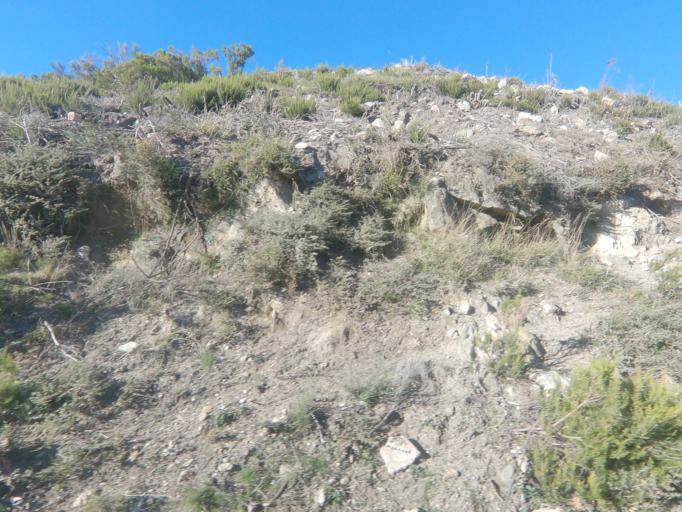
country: PT
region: Vila Real
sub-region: Vila Real
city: Vila Real
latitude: 41.3497
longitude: -7.7642
